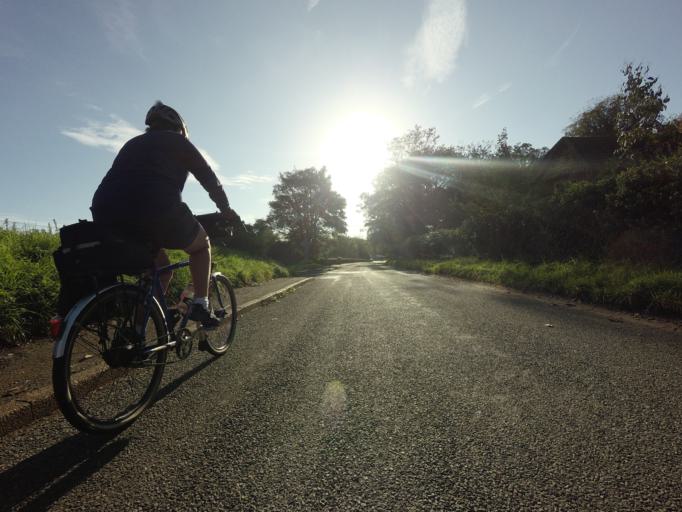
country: GB
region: England
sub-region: Norfolk
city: Dersingham
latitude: 52.8348
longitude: 0.5839
